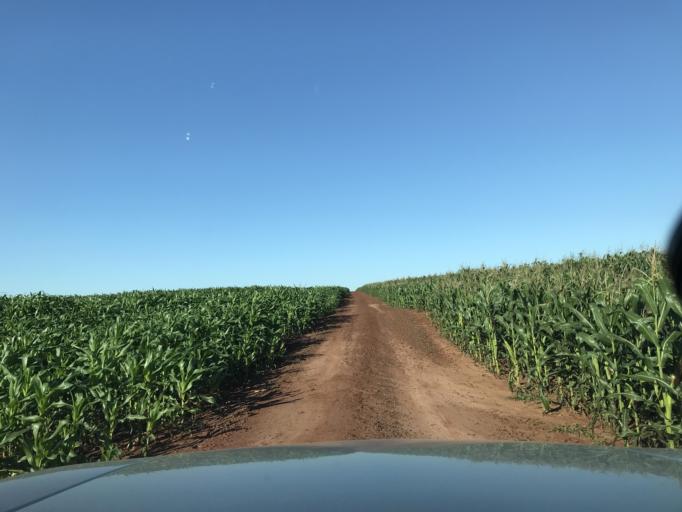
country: BR
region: Parana
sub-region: Palotina
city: Palotina
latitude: -24.2283
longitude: -53.7615
